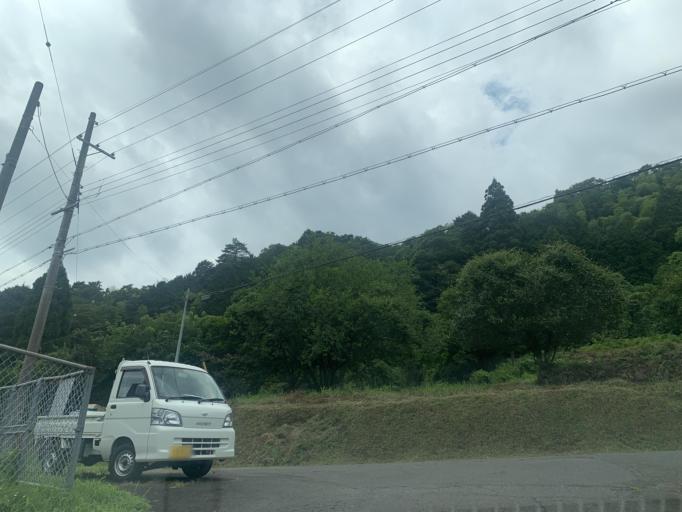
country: JP
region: Kyoto
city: Miyazu
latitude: 35.4472
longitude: 135.1607
